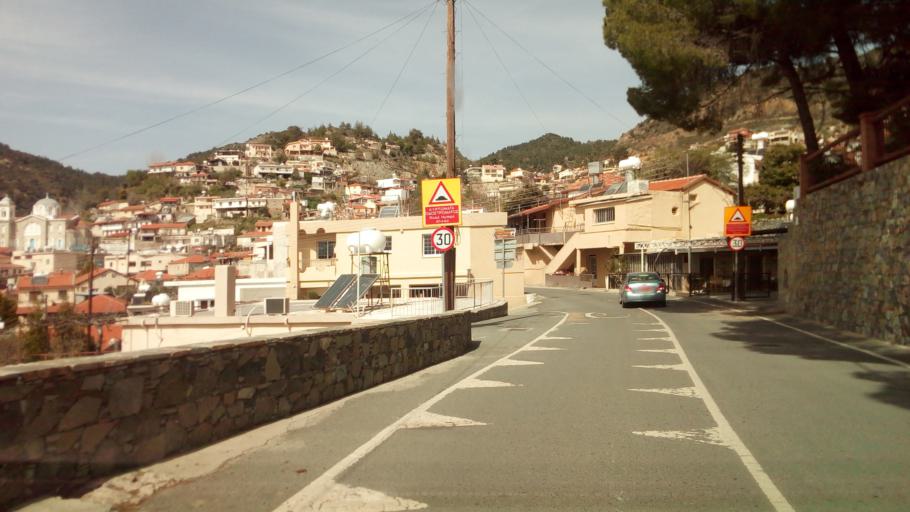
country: CY
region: Limassol
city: Pelendri
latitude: 34.8944
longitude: 32.9671
